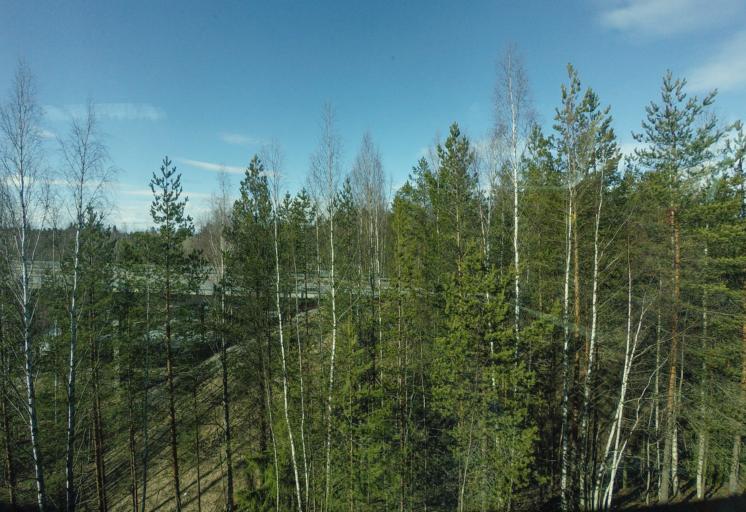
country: FI
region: South Karelia
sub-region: Lappeenranta
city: Lappeenranta
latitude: 61.0782
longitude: 28.2941
